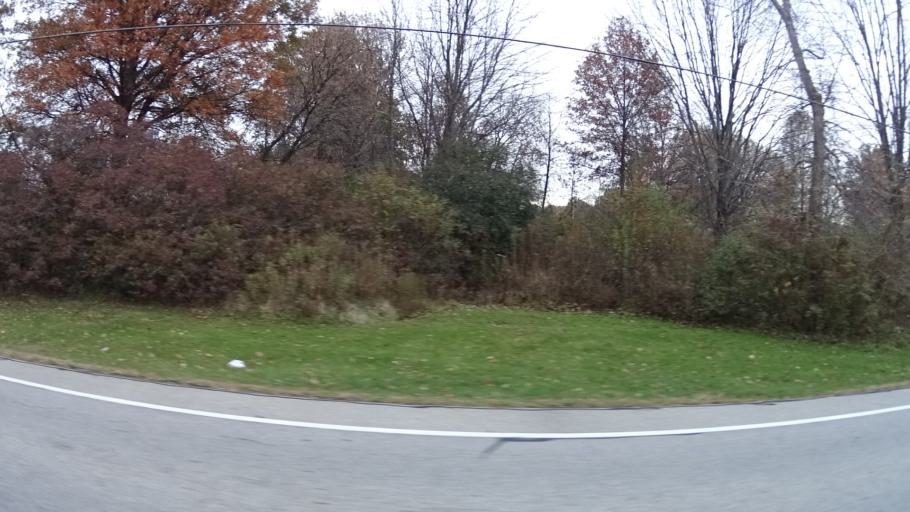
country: US
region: Ohio
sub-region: Lorain County
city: Elyria
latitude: 41.3286
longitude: -82.1079
